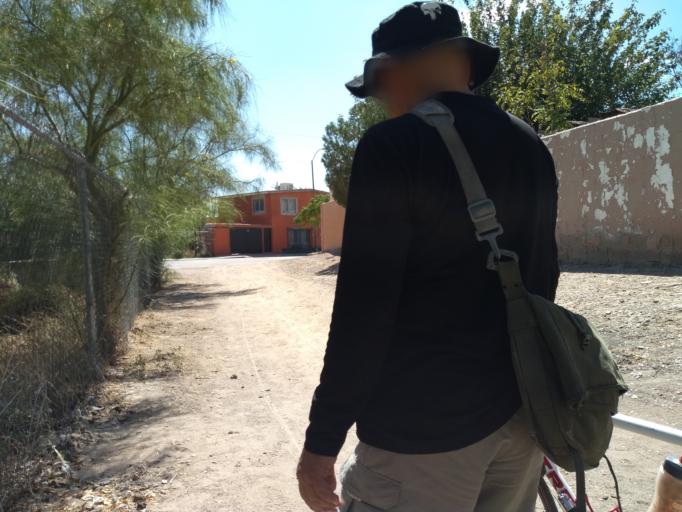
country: US
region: Texas
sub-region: El Paso County
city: El Paso
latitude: 31.7463
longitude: -106.4921
